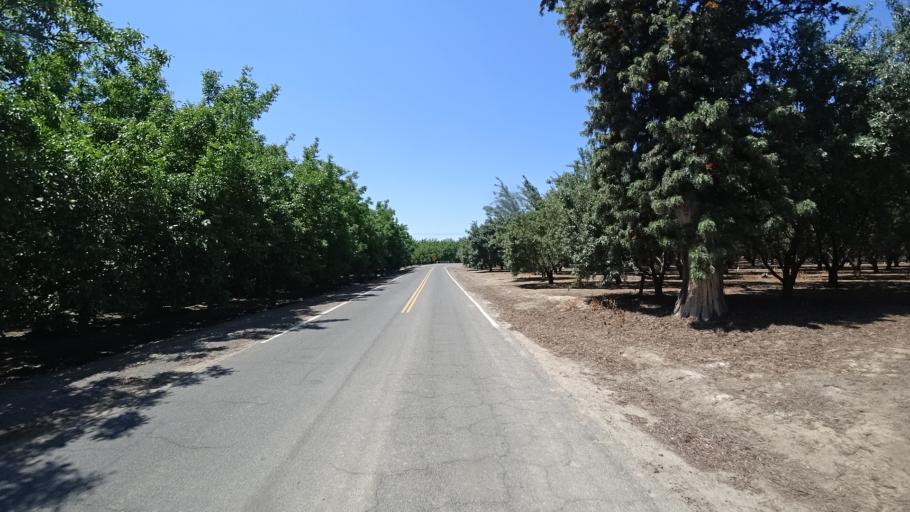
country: US
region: California
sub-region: Fresno County
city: Kingsburg
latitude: 36.4822
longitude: -119.5676
